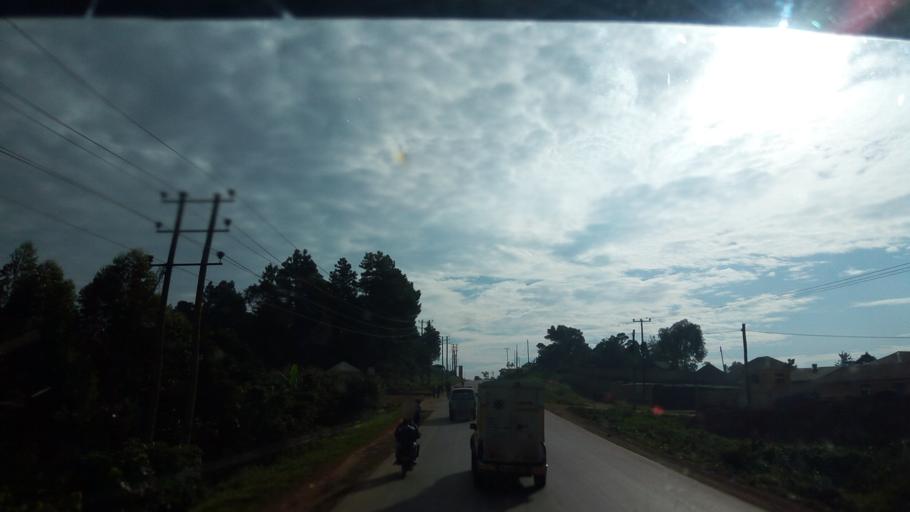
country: UG
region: Central Region
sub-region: Wakiso District
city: Wakiso
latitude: 0.4470
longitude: 32.5290
